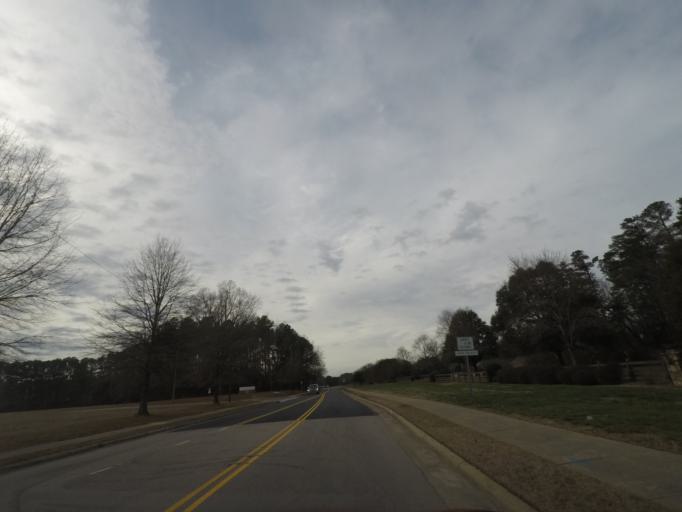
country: US
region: North Carolina
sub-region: Durham County
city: Durham
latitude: 36.0375
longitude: -78.9361
